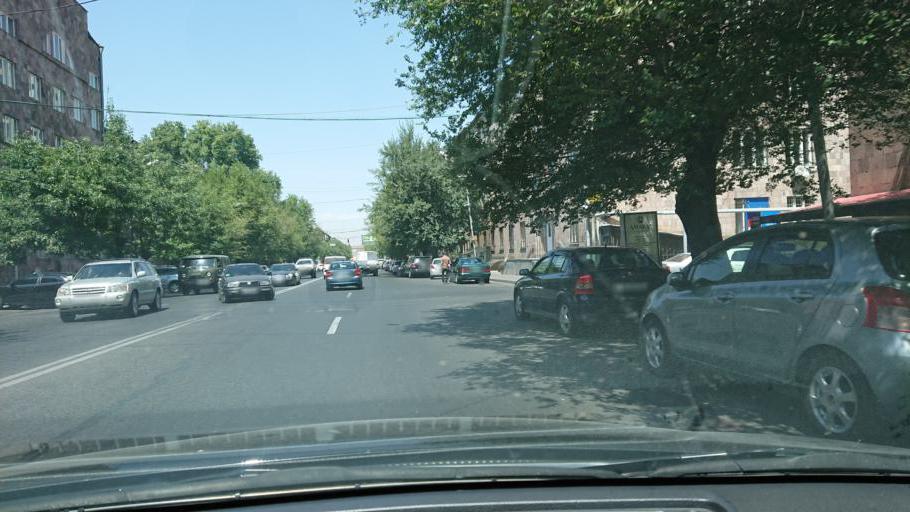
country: AM
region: Yerevan
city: Yerevan
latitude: 40.2016
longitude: 44.4995
